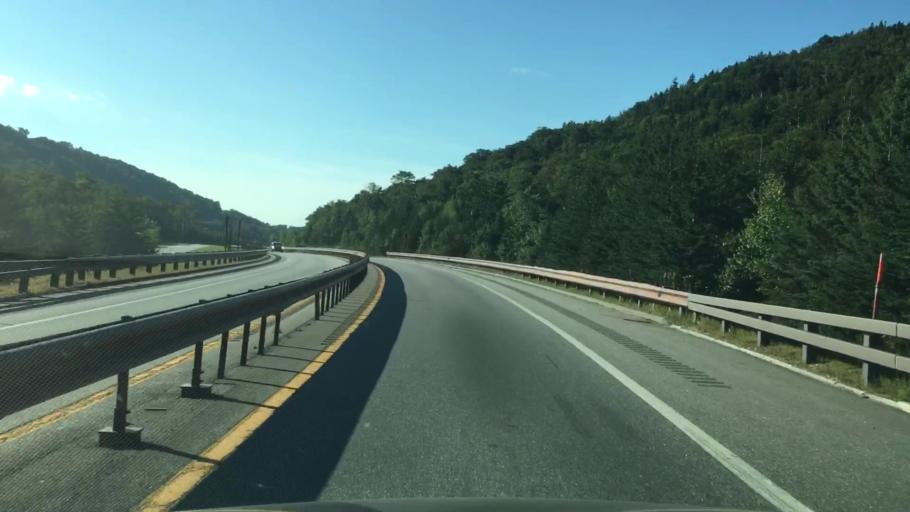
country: US
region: New Hampshire
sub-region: Grafton County
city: Deerfield
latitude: 44.1702
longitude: -71.6839
